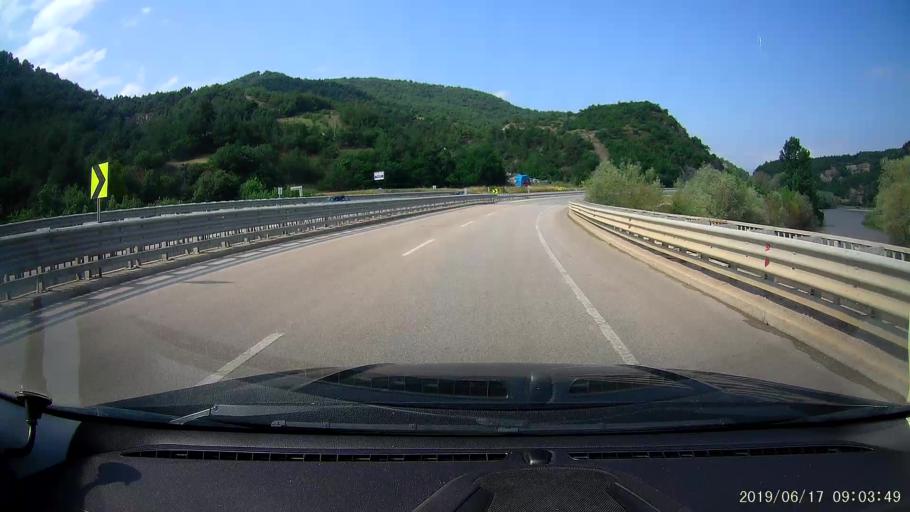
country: TR
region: Amasya
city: Tasova
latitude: 40.7501
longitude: 36.3012
